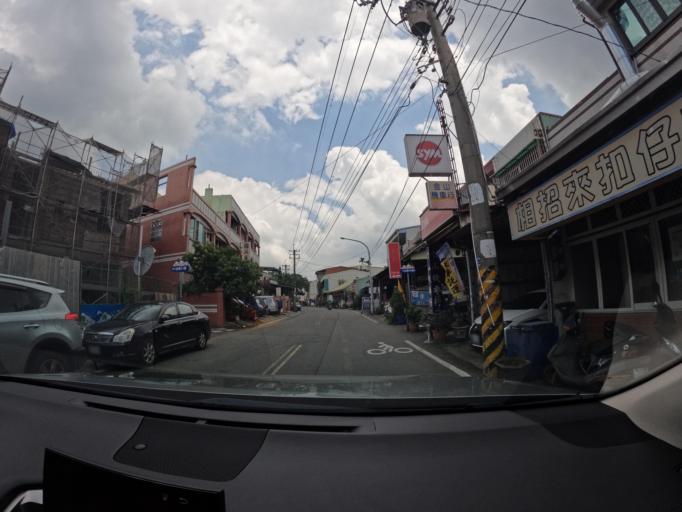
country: TW
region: Taiwan
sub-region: Nantou
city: Nantou
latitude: 23.9080
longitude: 120.6386
